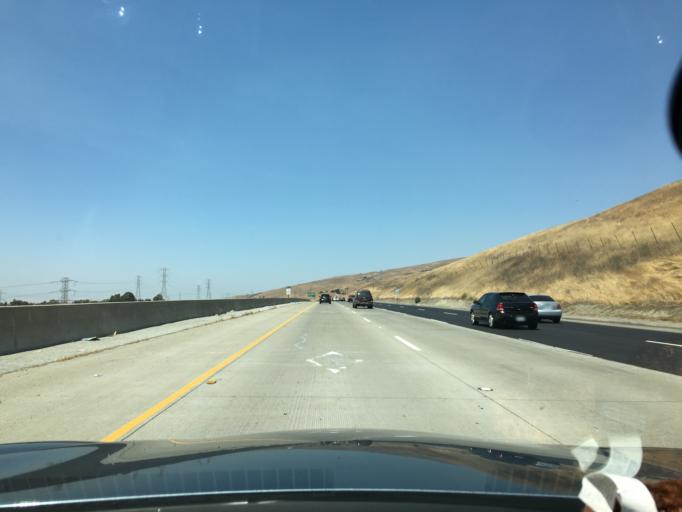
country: US
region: California
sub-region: Santa Clara County
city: Morgan Hill
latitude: 37.1818
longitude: -121.6825
